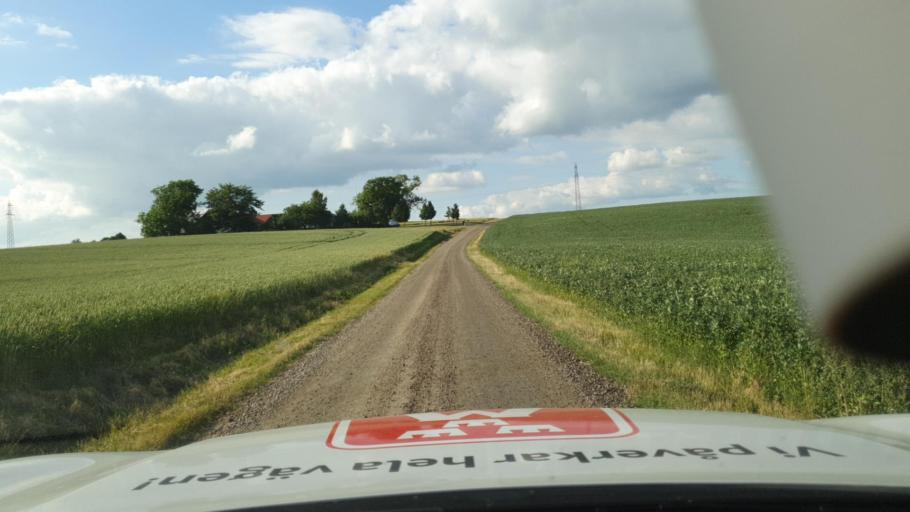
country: SE
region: Skane
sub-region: Skurups Kommun
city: Rydsgard
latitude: 55.4989
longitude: 13.5769
